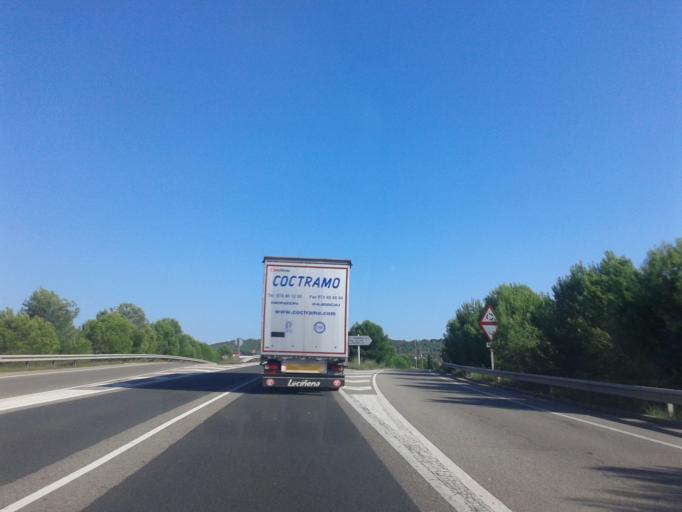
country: ES
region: Catalonia
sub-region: Provincia de Tarragona
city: El Vendrell
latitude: 41.2316
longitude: 1.5380
